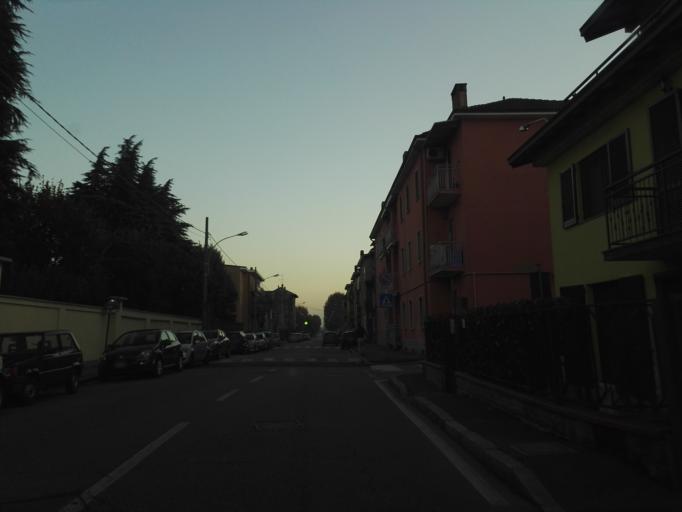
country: IT
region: Lombardy
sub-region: Citta metropolitana di Milano
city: Mezzate
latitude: 45.4463
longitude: 9.2939
